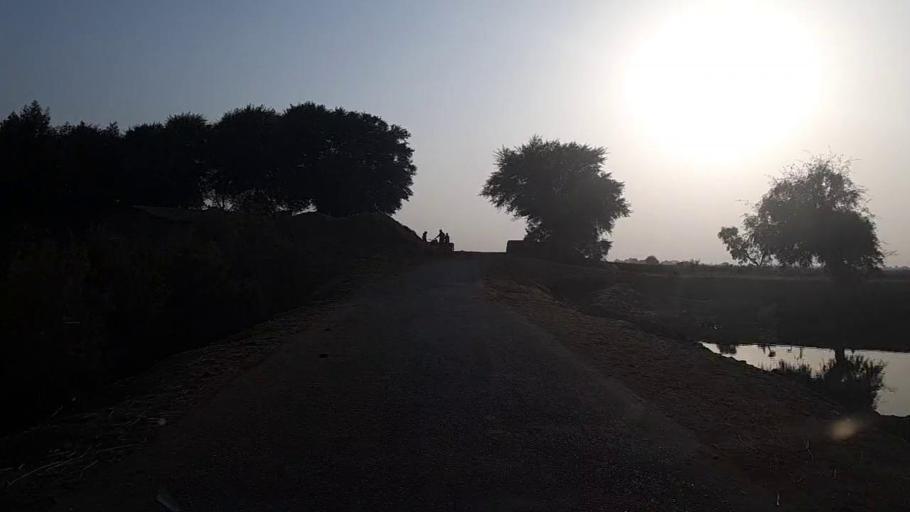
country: PK
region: Sindh
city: Ghauspur
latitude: 28.2328
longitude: 69.0876
